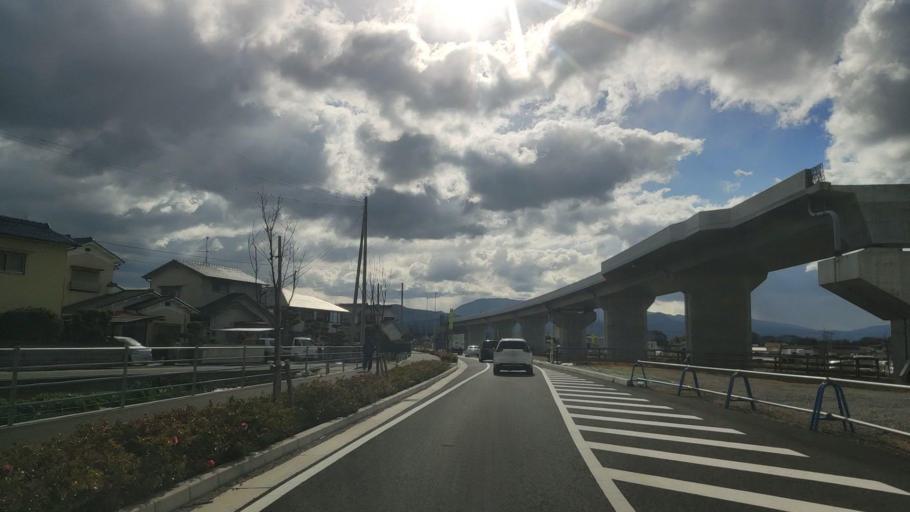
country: JP
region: Ehime
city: Masaki-cho
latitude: 33.8154
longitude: 132.7203
